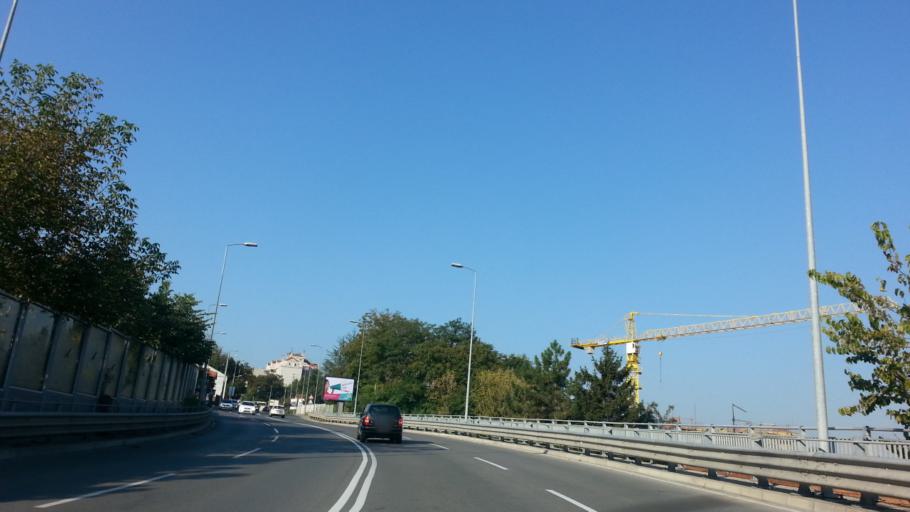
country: RS
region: Central Serbia
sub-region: Belgrade
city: Cukarica
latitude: 44.7844
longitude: 20.4262
